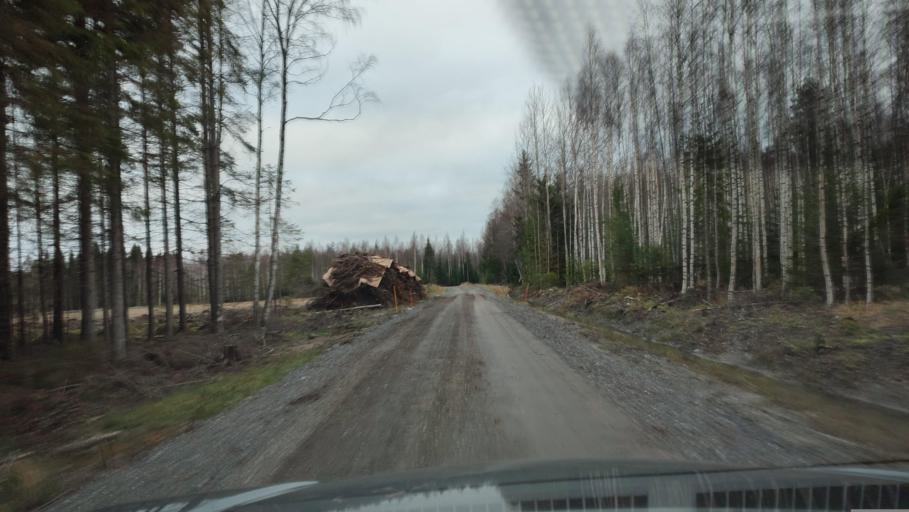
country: FI
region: Southern Ostrobothnia
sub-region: Suupohja
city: Karijoki
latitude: 62.2175
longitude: 21.6012
